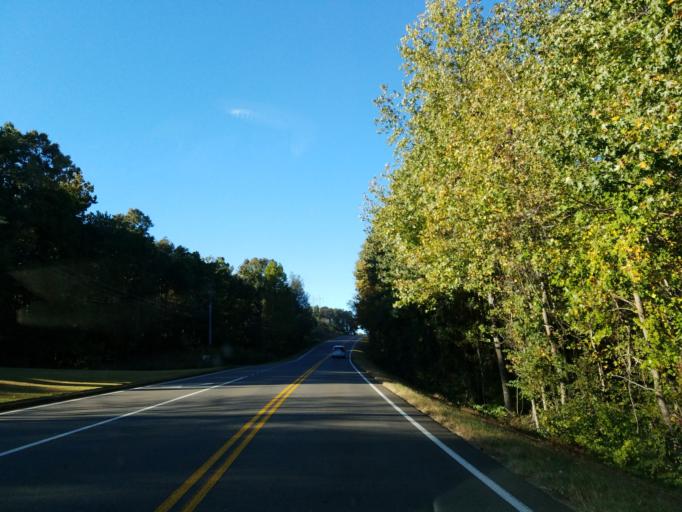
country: US
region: Georgia
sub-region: Pickens County
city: Nelson
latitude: 34.3957
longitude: -84.3818
